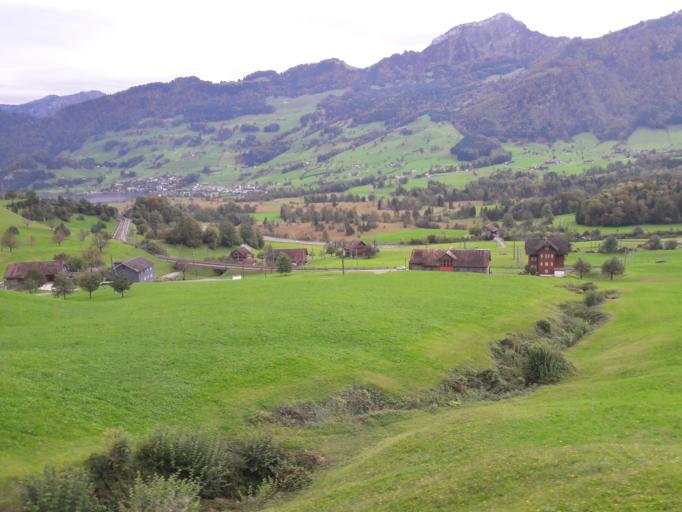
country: CH
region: Schwyz
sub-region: Bezirk Schwyz
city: Goldau
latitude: 47.0544
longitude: 8.5727
